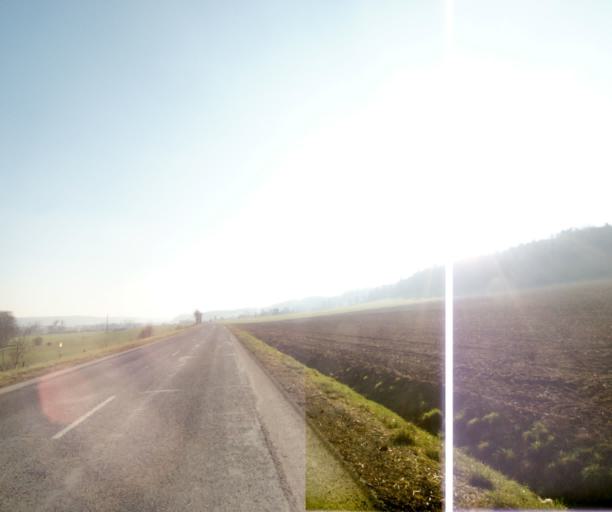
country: FR
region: Champagne-Ardenne
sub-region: Departement de la Haute-Marne
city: Chevillon
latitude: 48.5144
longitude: 5.1105
